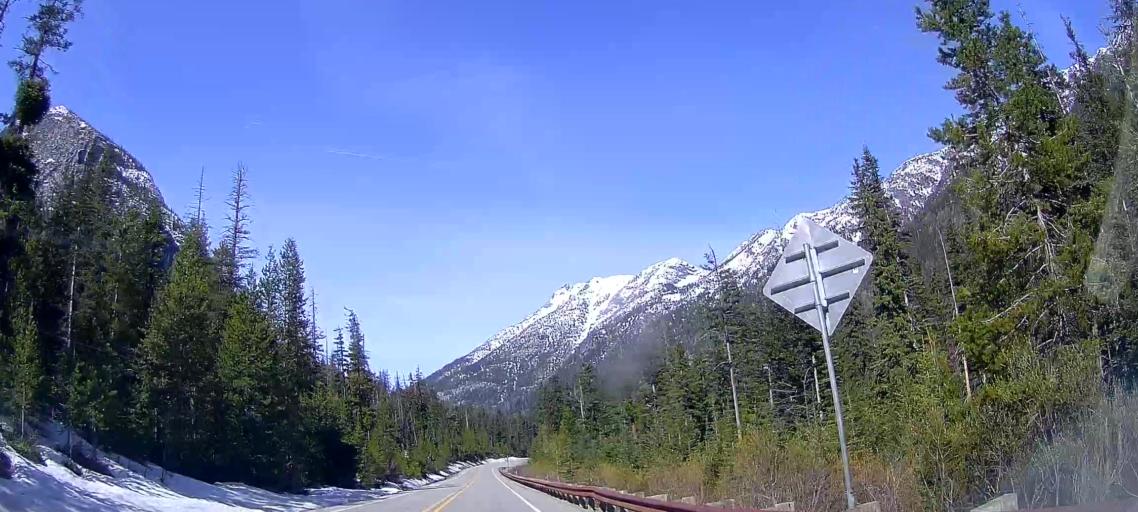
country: US
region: Washington
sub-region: Chelan County
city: Granite Falls
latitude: 48.5991
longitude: -120.5782
